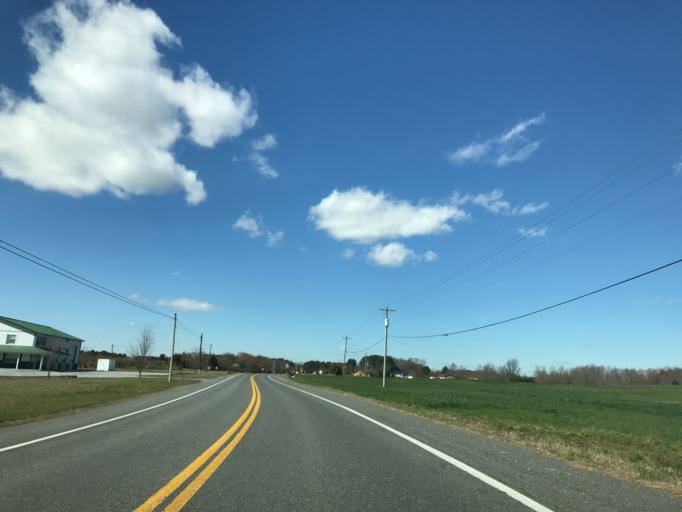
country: US
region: Maryland
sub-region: Queen Anne's County
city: Kingstown
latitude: 39.1519
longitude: -75.9790
